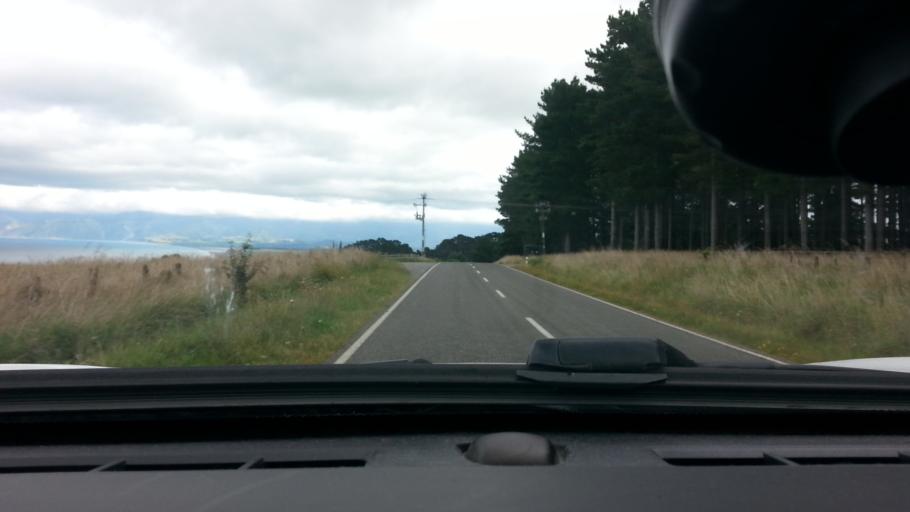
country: NZ
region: Wellington
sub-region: South Wairarapa District
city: Waipawa
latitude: -41.4343
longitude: 175.2266
